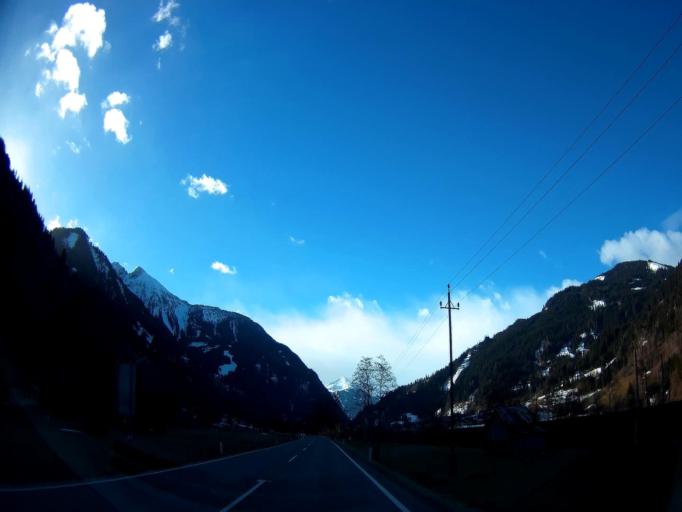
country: AT
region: Salzburg
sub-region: Politischer Bezirk Sankt Johann im Pongau
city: Dorfgastein
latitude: 47.2275
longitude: 13.1076
